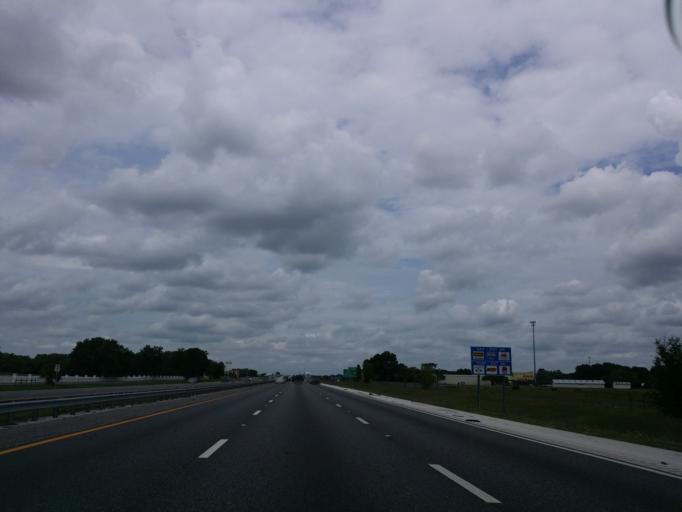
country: US
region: Florida
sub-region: Marion County
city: Belleview
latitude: 29.0179
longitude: -82.1551
